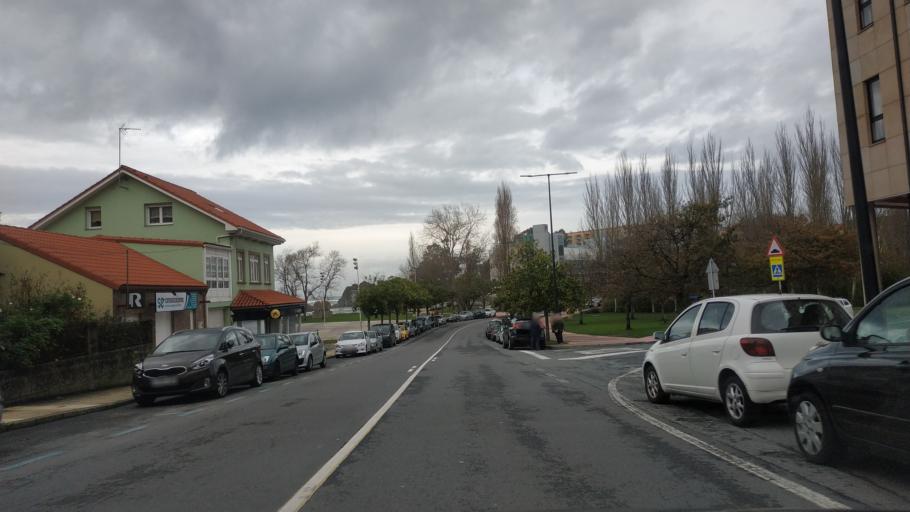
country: ES
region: Galicia
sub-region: Provincia da Coruna
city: Oleiros
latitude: 43.3471
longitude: -8.3458
